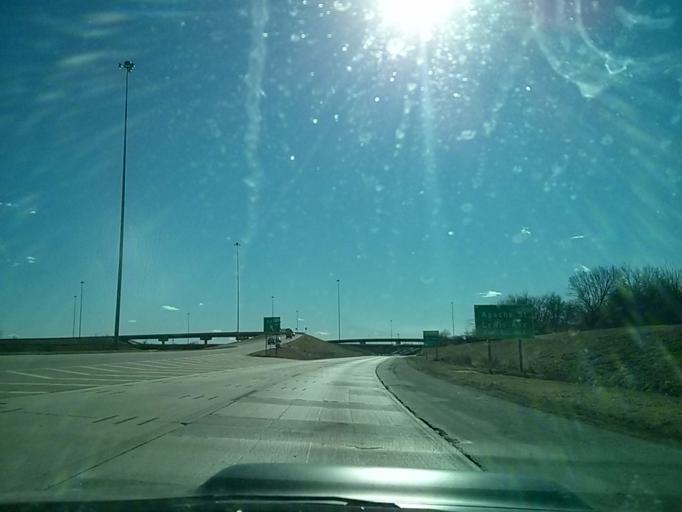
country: US
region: Oklahoma
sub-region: Tulsa County
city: Turley
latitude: 36.2041
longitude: -95.9475
